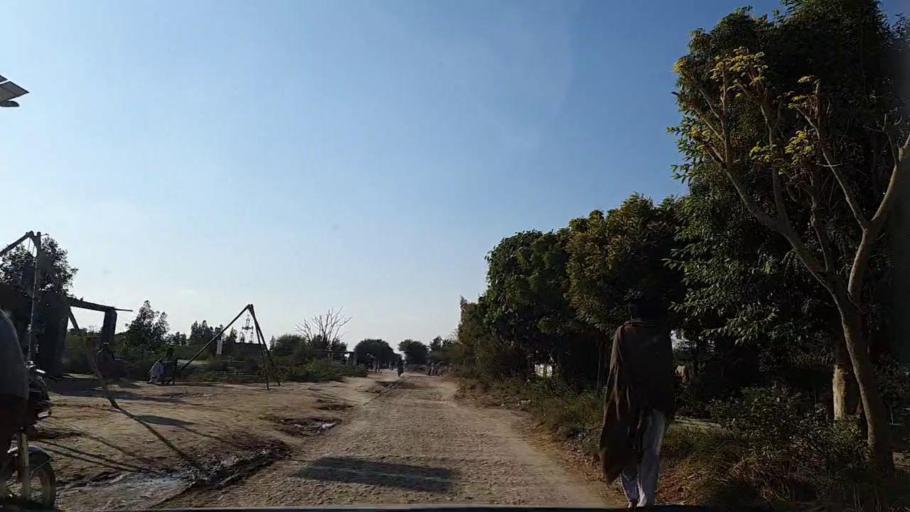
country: PK
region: Sindh
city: Pithoro
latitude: 25.6462
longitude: 69.3472
